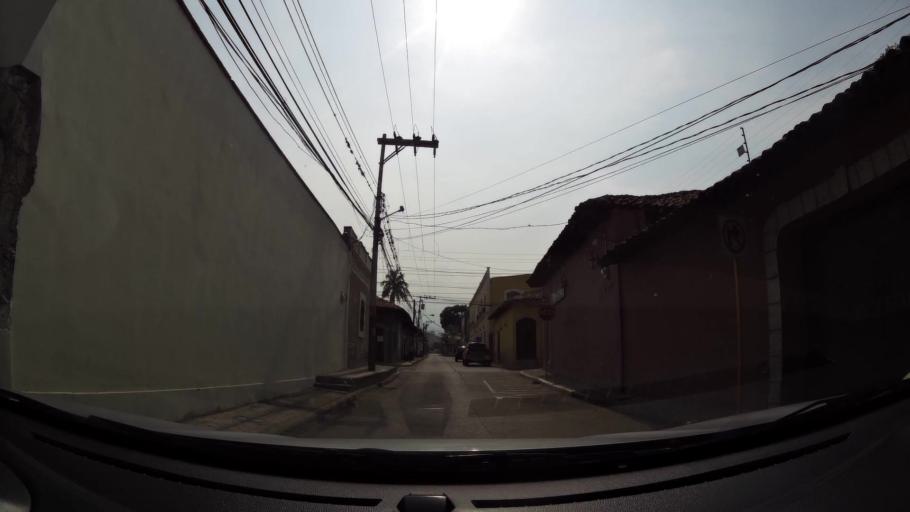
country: HN
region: Comayagua
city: Comayagua
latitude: 14.4611
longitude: -87.6431
